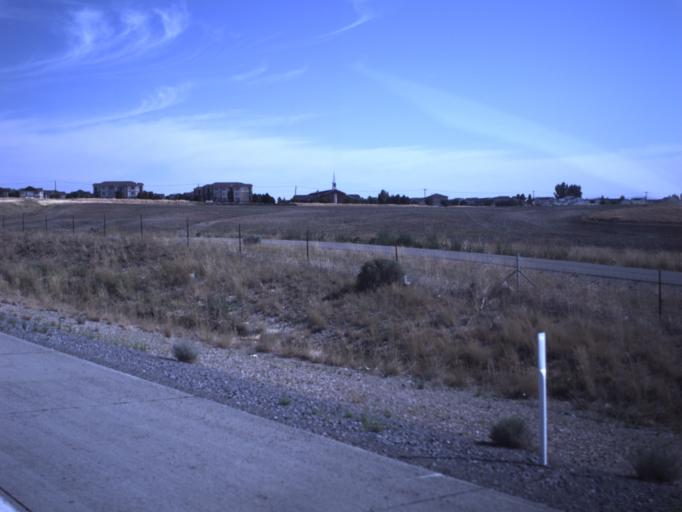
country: US
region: Utah
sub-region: Salt Lake County
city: Oquirrh
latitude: 40.6192
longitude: -112.0421
